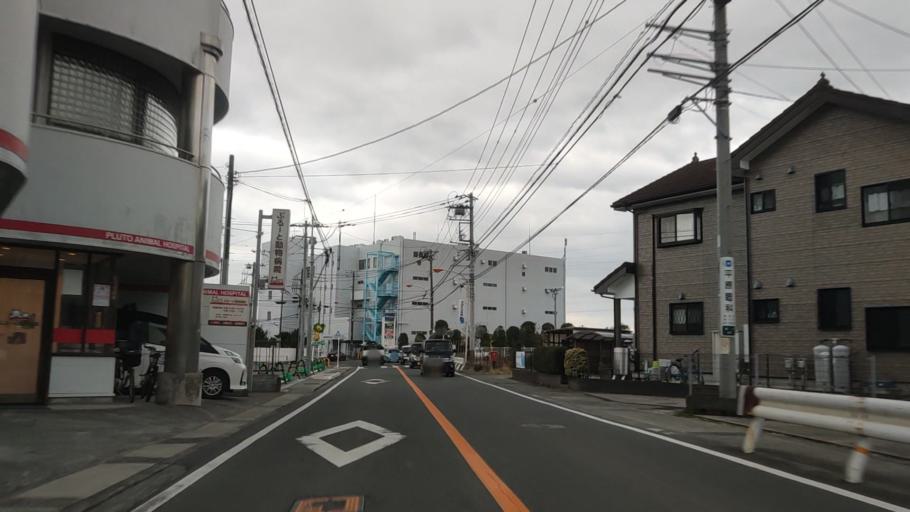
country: JP
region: Kanagawa
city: Odawara
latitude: 35.2840
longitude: 139.1933
